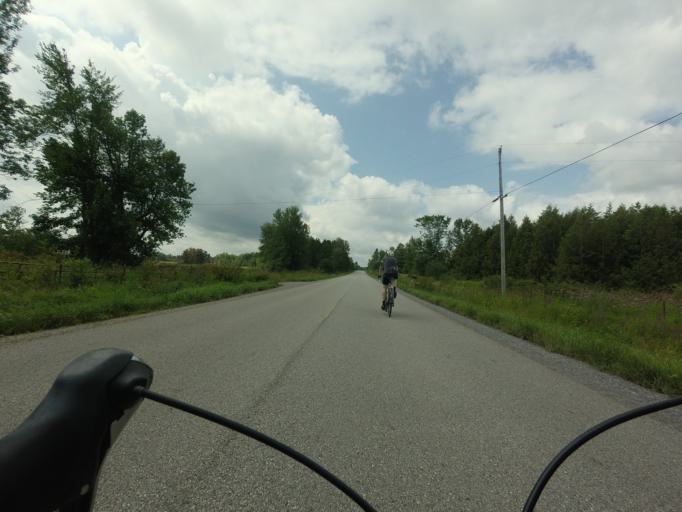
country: CA
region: Ontario
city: Prescott
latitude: 44.8099
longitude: -75.7122
